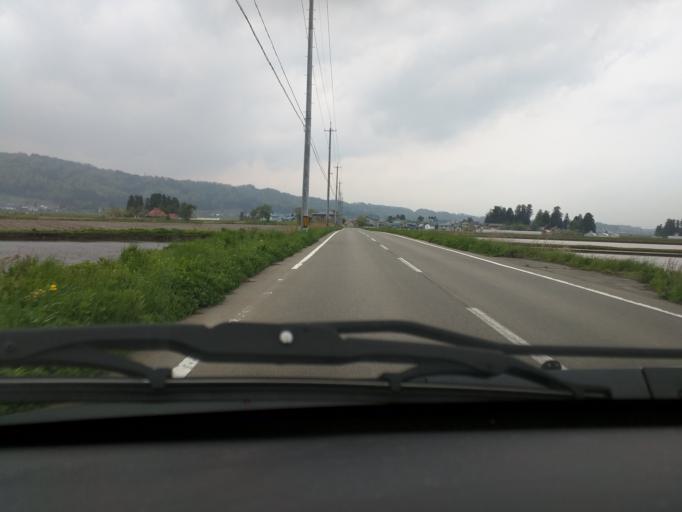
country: JP
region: Fukushima
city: Kitakata
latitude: 37.4733
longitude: 139.8335
